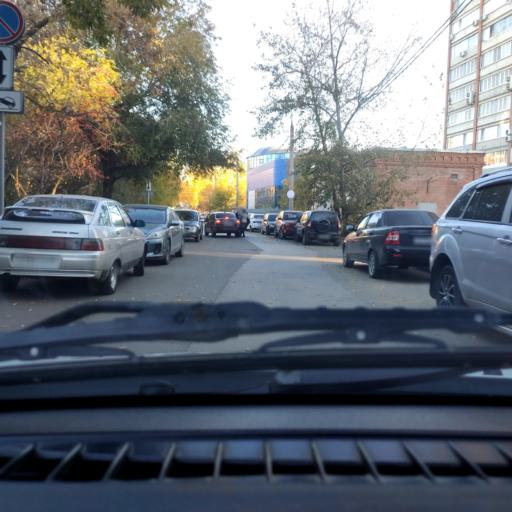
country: RU
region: Samara
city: Zhigulevsk
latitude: 53.4803
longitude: 49.4715
